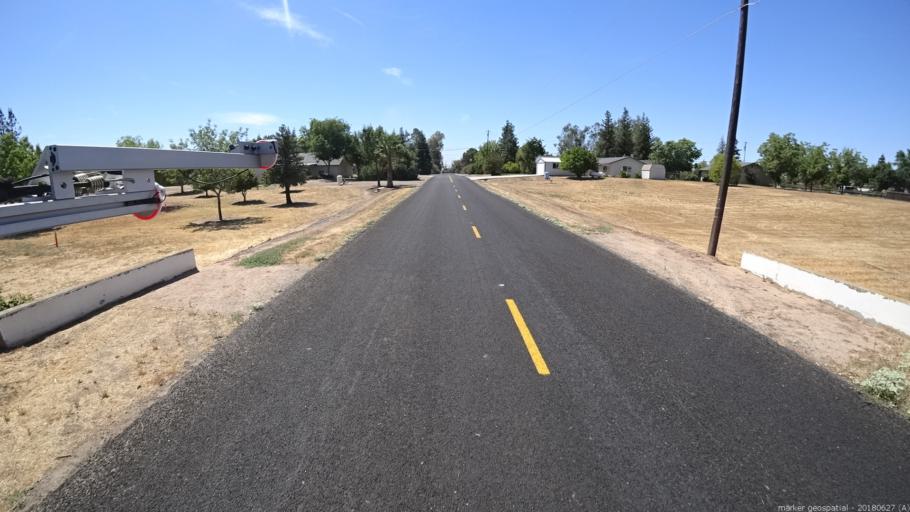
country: US
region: California
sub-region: Madera County
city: Bonadelle Ranchos-Madera Ranchos
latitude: 36.9202
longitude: -119.8820
